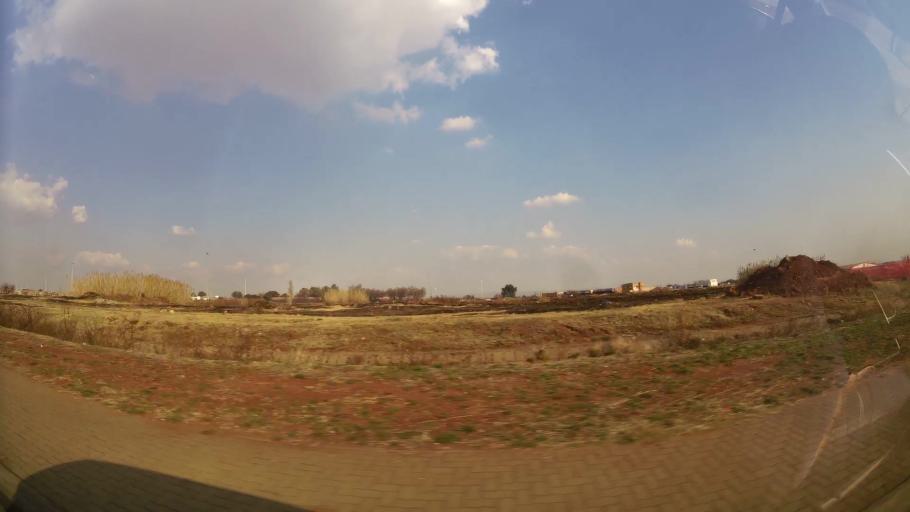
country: ZA
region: Gauteng
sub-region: Ekurhuleni Metropolitan Municipality
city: Germiston
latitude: -26.3447
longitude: 28.1878
